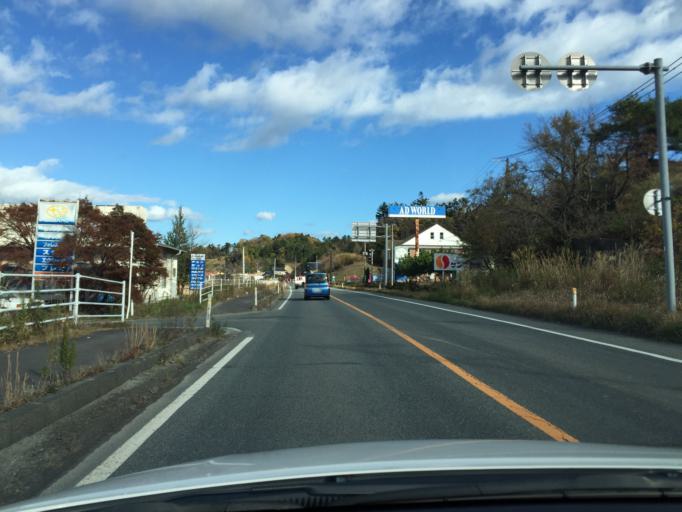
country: JP
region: Fukushima
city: Namie
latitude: 37.5384
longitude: 141.0064
